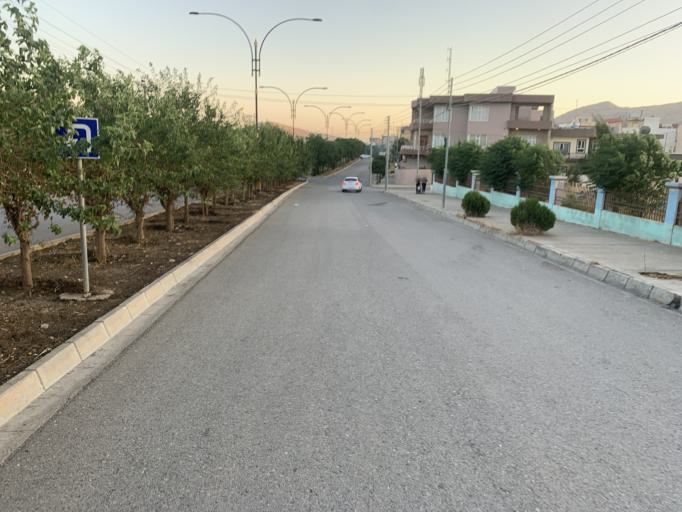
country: IQ
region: As Sulaymaniyah
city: Raniye
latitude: 36.2428
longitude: 44.8762
